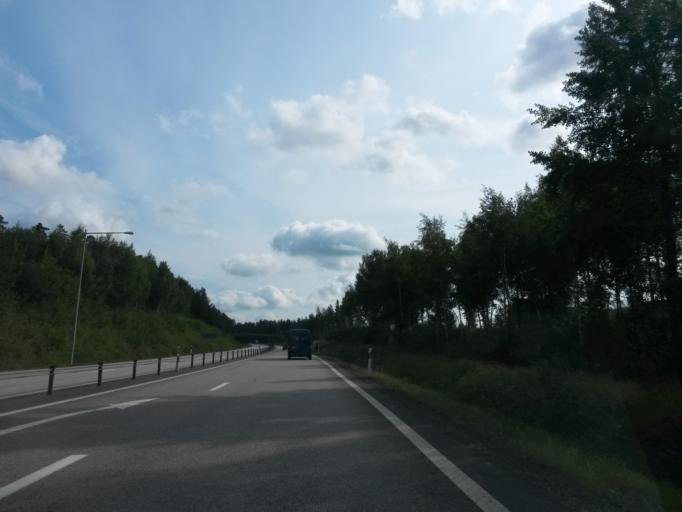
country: SE
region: Kronoberg
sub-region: Vaxjo Kommun
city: Vaexjoe
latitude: 56.8916
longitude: 14.7625
